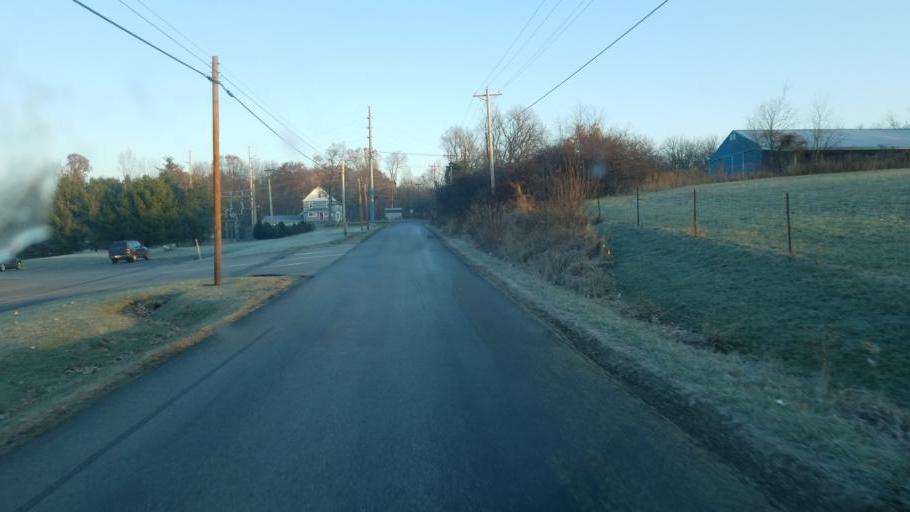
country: US
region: Ohio
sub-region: Medina County
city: Lodi
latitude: 41.0249
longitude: -81.9958
